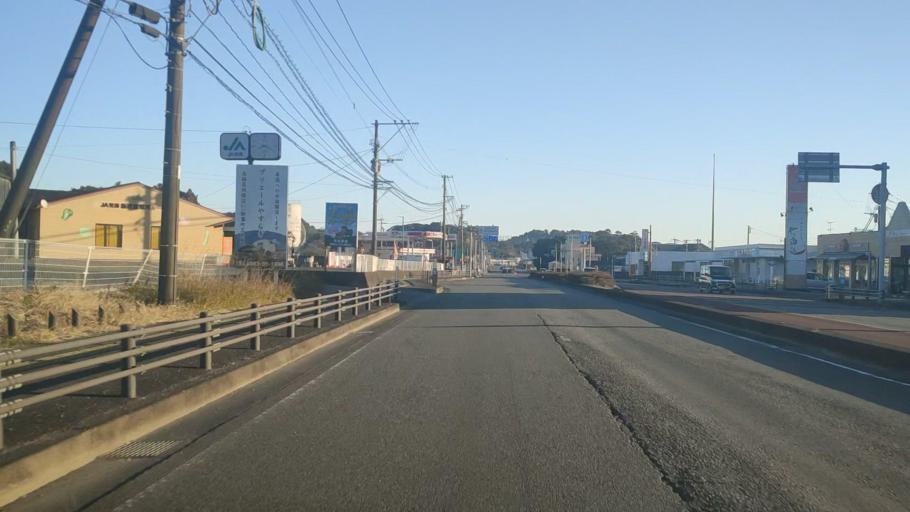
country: JP
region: Miyazaki
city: Takanabe
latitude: 32.0692
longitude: 131.4893
